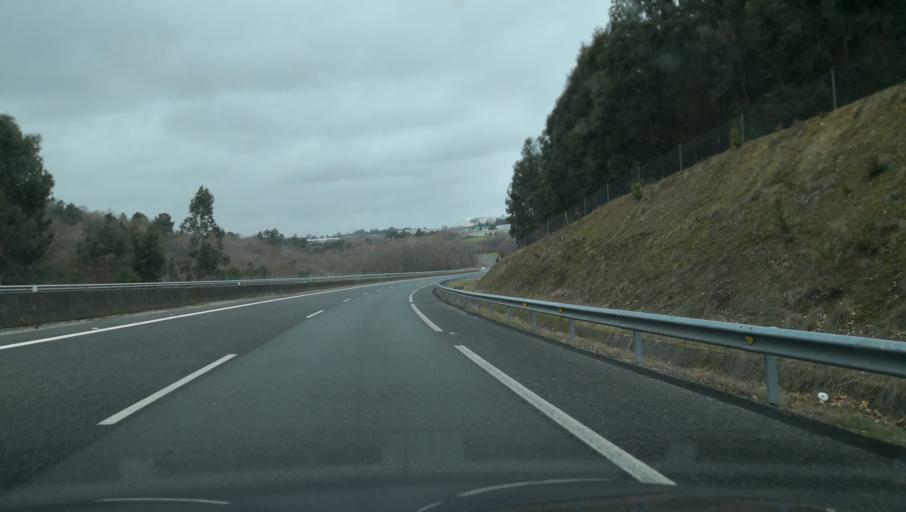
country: ES
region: Galicia
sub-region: Provincia de Pontevedra
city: Lalin
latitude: 42.6630
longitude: -8.1460
